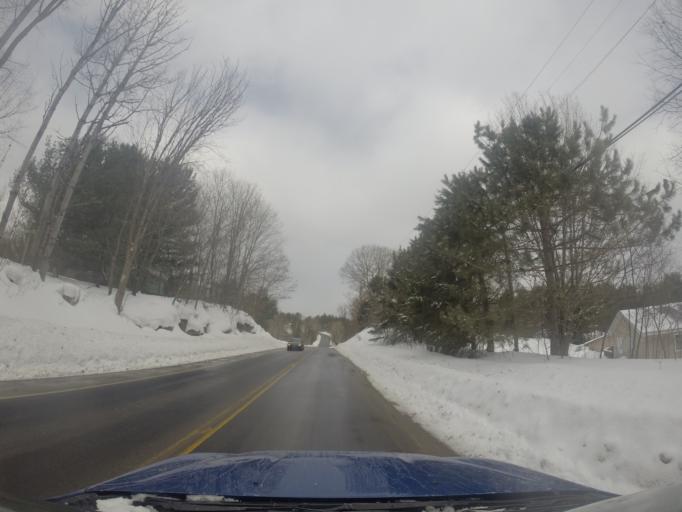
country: CA
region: Ontario
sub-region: Parry Sound District
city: Parry Sound
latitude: 45.3865
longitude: -80.0268
